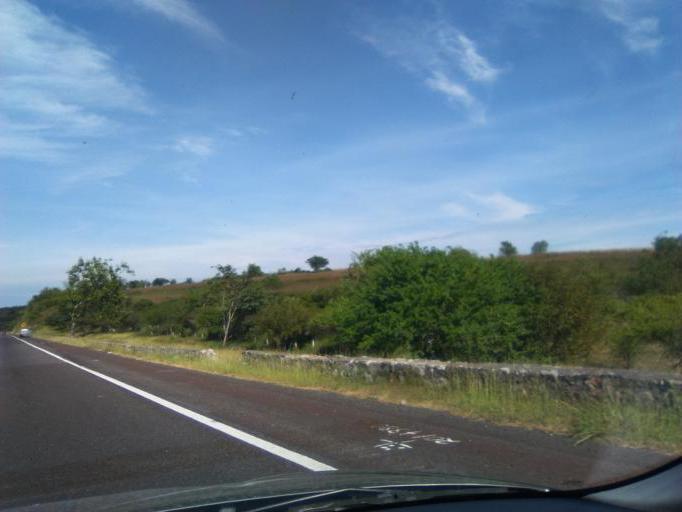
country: MX
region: Guerrero
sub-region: Huitzuco de los Figueroa
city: San Francisco Ozomatlan
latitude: 18.0484
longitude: -99.2557
